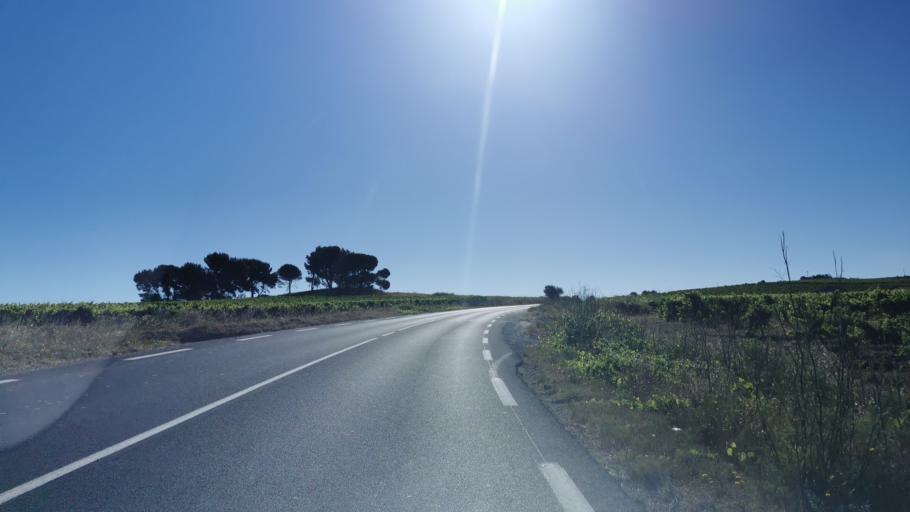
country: FR
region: Languedoc-Roussillon
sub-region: Departement de l'Herault
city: Nissan-lez-Enserune
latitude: 43.2765
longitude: 3.0820
